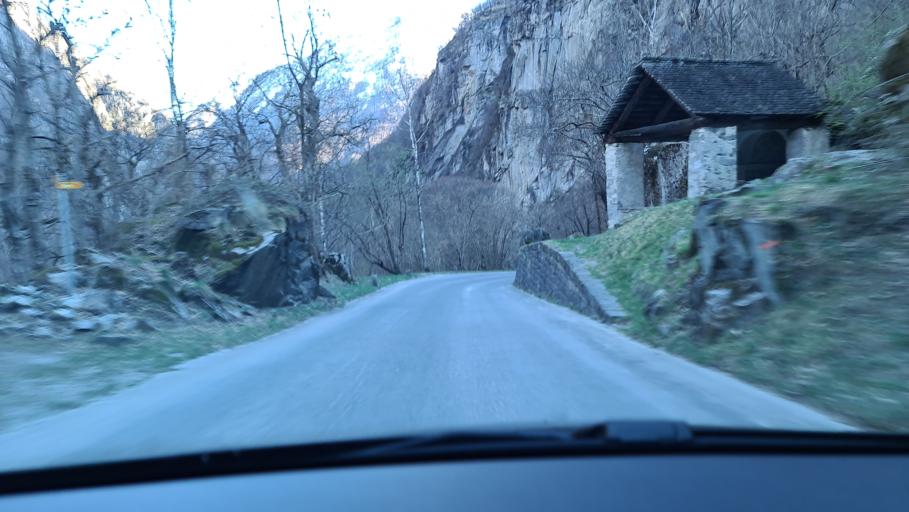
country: CH
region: Ticino
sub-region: Vallemaggia District
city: Cevio
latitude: 46.4000
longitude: 8.5326
